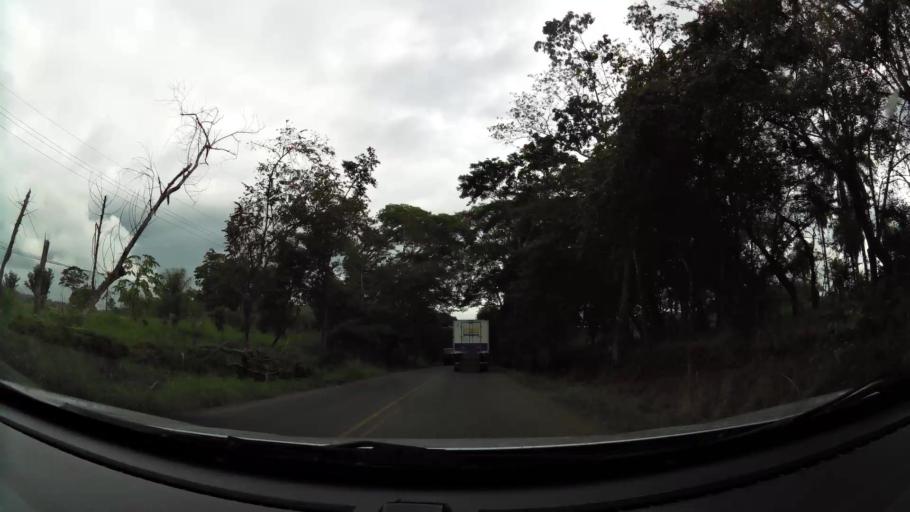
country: CR
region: Guanacaste
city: Juntas
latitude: 10.1672
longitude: -84.9205
